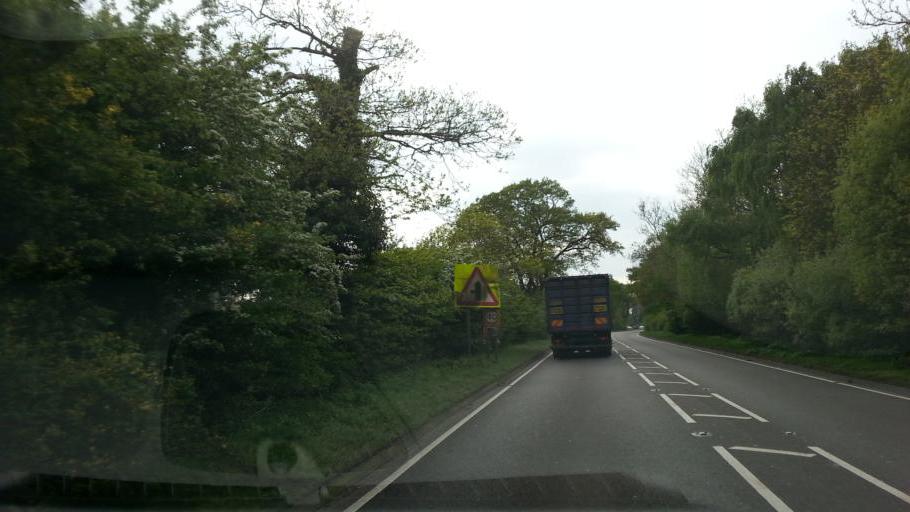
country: GB
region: England
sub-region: Nottinghamshire
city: South Collingham
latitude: 53.0811
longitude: -0.7218
